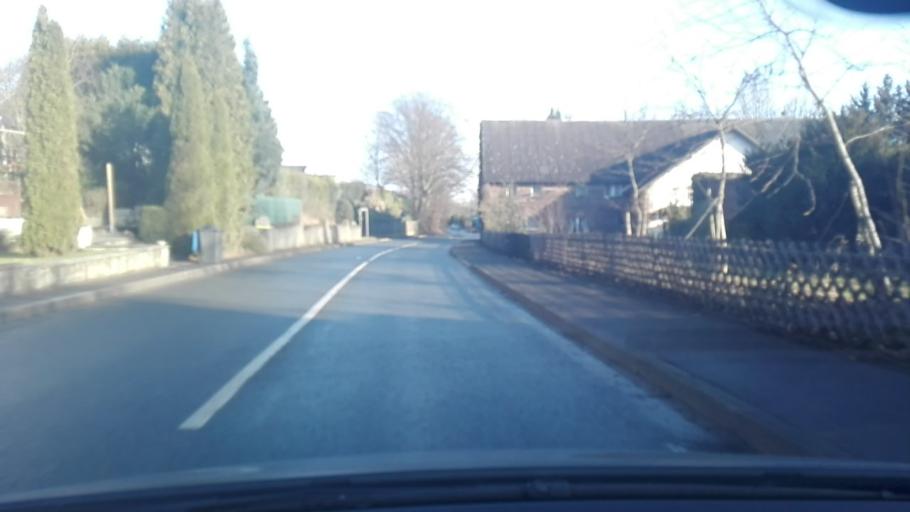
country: DE
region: North Rhine-Westphalia
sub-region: Regierungsbezirk Arnsberg
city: Frondenberg
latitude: 51.5140
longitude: 7.7712
